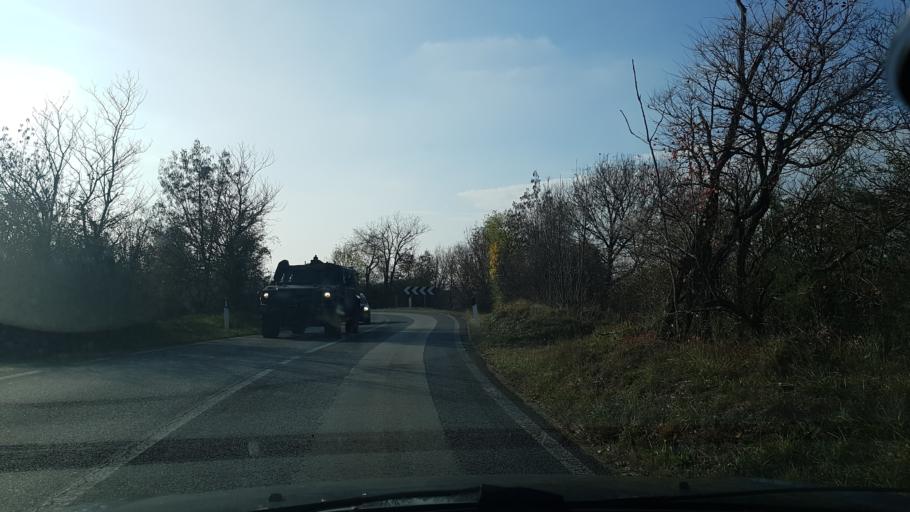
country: IT
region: Friuli Venezia Giulia
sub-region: Provincia di Gorizia
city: Doberdo del Lago
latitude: 45.8373
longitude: 13.5247
